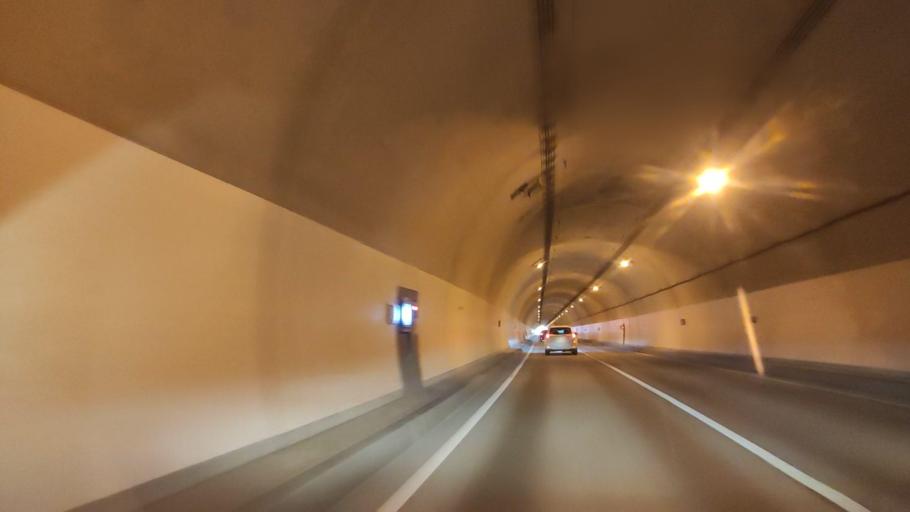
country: JP
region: Hokkaido
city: Ishikari
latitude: 43.4765
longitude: 141.3951
